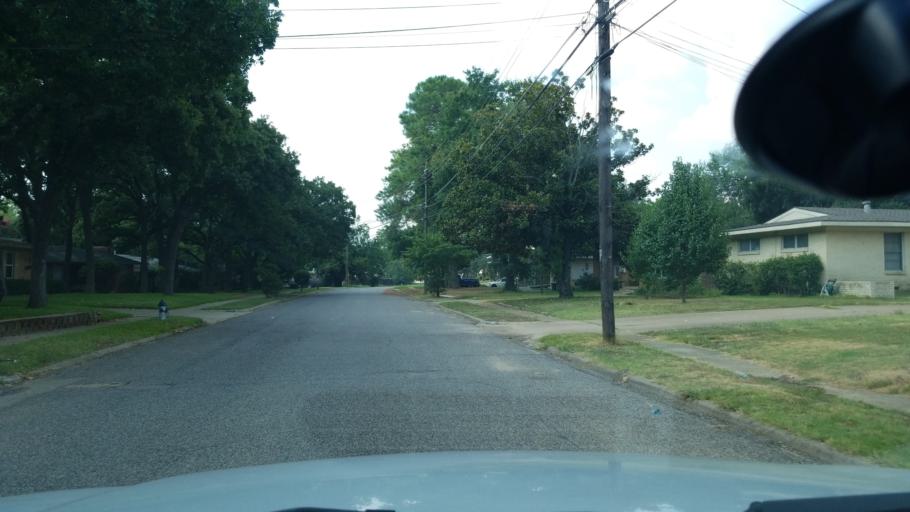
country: US
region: Texas
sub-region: Dallas County
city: Irving
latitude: 32.8323
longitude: -96.9243
